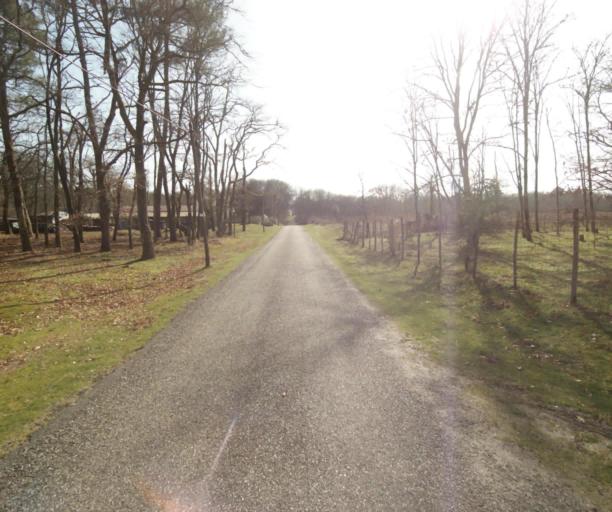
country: FR
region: Aquitaine
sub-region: Departement des Landes
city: Roquefort
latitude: 44.1251
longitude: -0.1917
